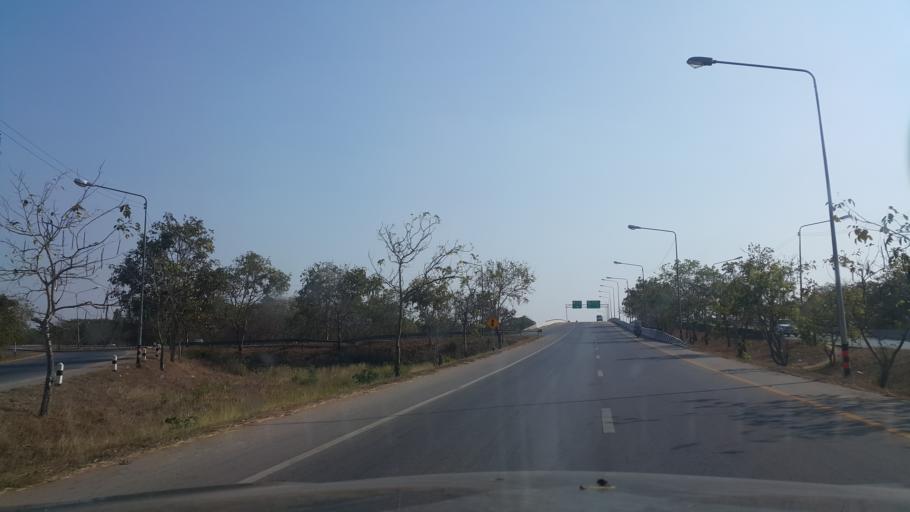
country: TH
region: Khon Kaen
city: Khon Kaen
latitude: 16.4402
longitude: 102.9181
